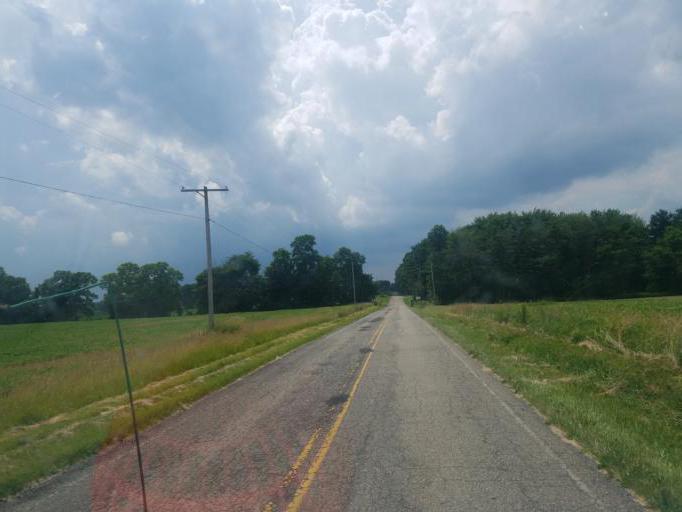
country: US
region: Ohio
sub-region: Columbiana County
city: Salem
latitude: 40.9739
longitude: -80.8940
